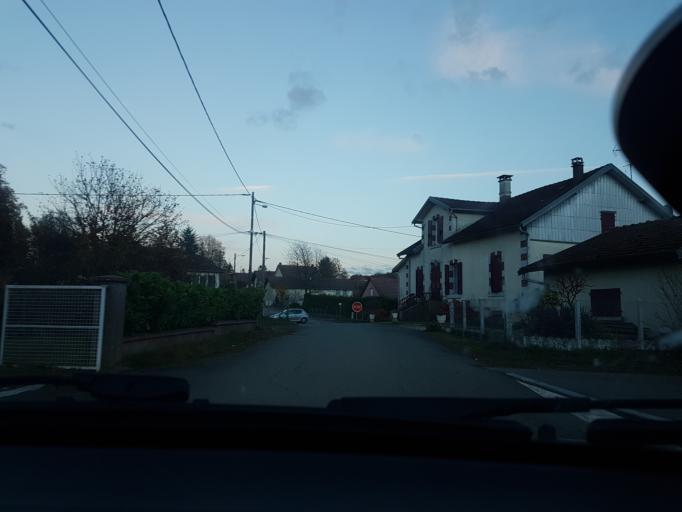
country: FR
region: Franche-Comte
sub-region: Departement de la Haute-Saone
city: Plancher-Bas
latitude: 47.7215
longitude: 6.7334
